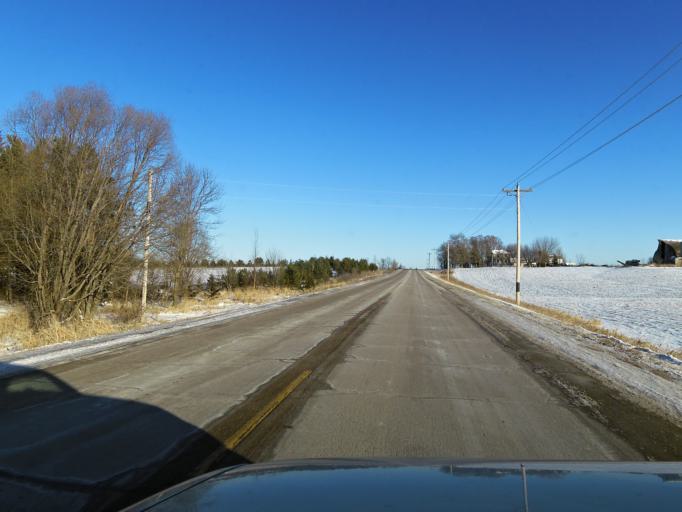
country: US
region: Minnesota
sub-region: Scott County
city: Jordan
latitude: 44.6499
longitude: -93.5625
